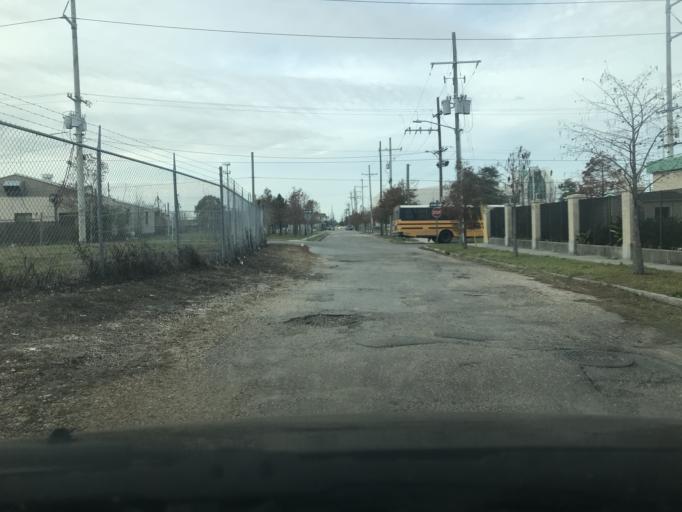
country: US
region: Louisiana
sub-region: Orleans Parish
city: New Orleans
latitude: 29.9618
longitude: -90.1080
